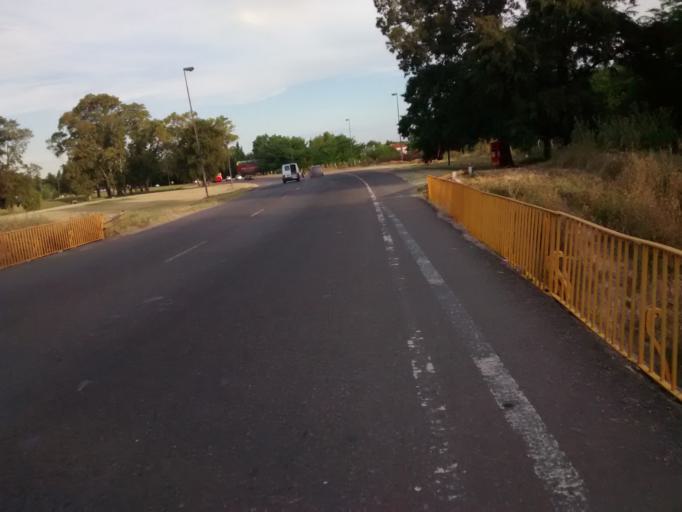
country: AR
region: Buenos Aires
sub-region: Partido de La Plata
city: La Plata
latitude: -34.8609
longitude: -58.0657
